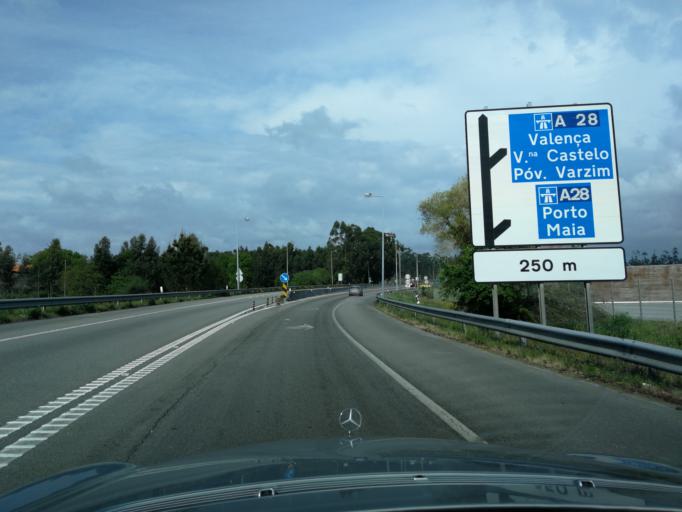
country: PT
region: Porto
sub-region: Vila do Conde
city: Vila do Conde
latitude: 41.3740
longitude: -8.7303
